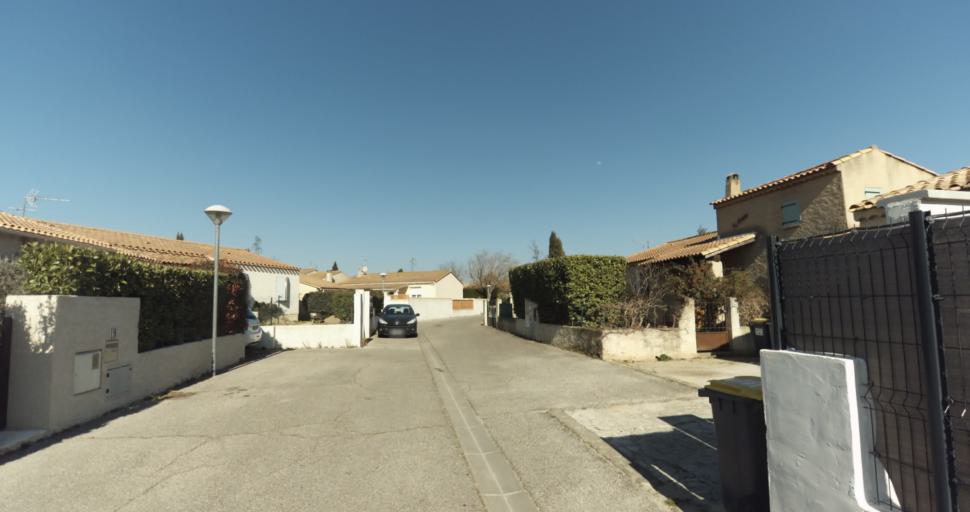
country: FR
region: Provence-Alpes-Cote d'Azur
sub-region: Departement des Bouches-du-Rhone
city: Pelissanne
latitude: 43.6375
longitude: 5.1394
